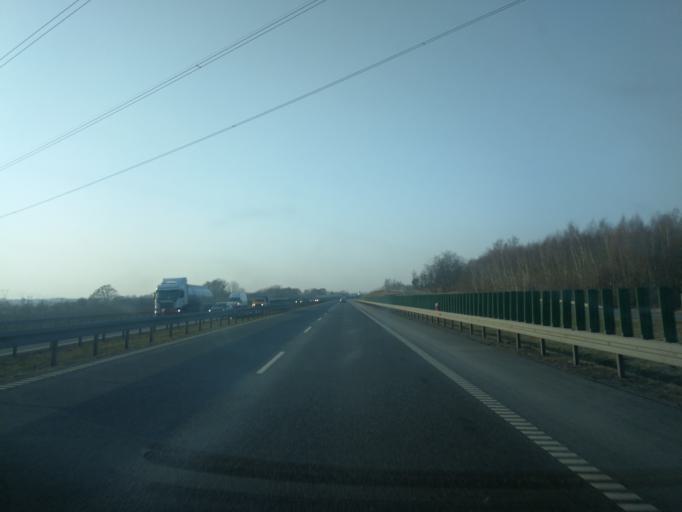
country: PL
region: Warmian-Masurian Voivodeship
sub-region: Powiat elblaski
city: Gronowo Gorne
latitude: 54.1200
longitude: 19.4711
